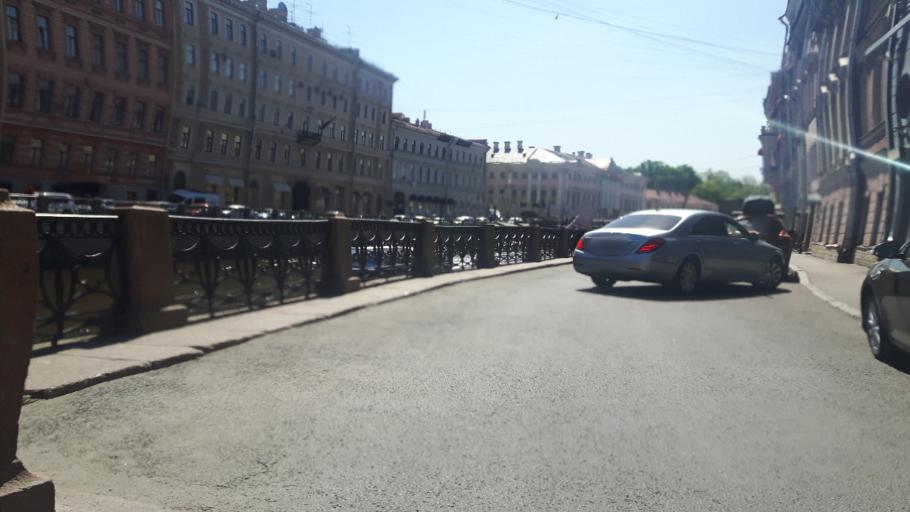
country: RU
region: St.-Petersburg
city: Saint Petersburg
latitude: 59.9374
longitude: 30.3194
